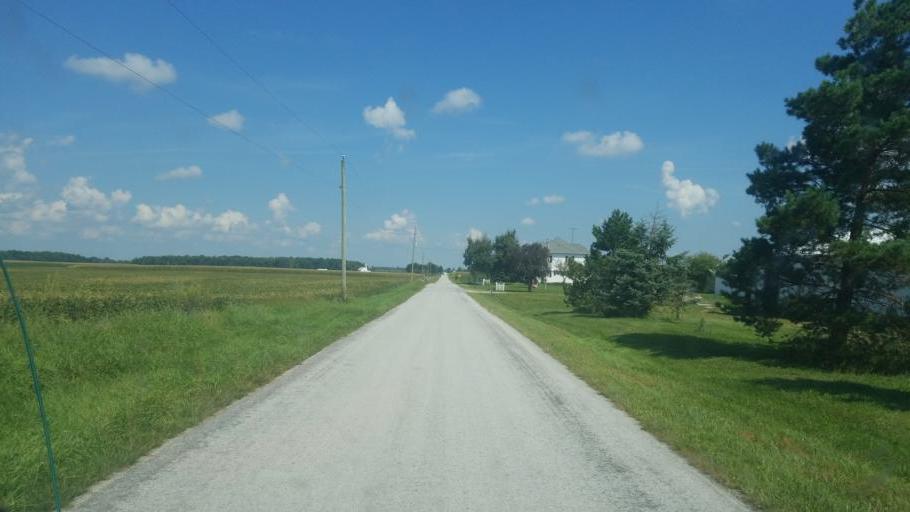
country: US
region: Ohio
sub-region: Hardin County
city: Kenton
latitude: 40.6765
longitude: -83.4957
